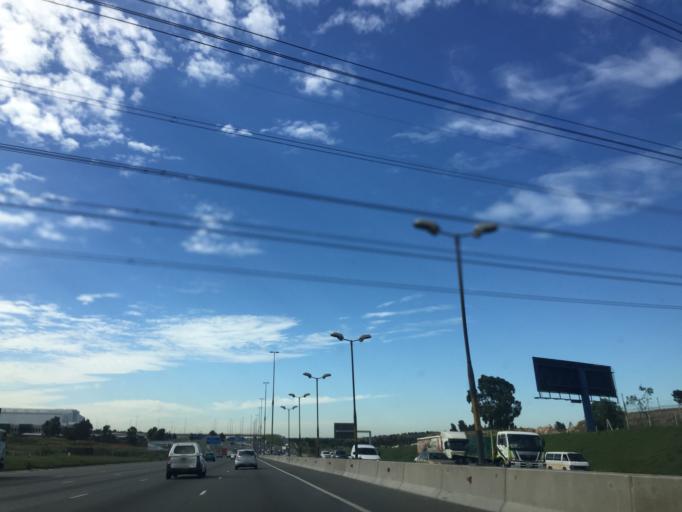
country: ZA
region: Gauteng
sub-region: Ekurhuleni Metropolitan Municipality
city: Germiston
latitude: -26.2288
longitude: 28.1261
